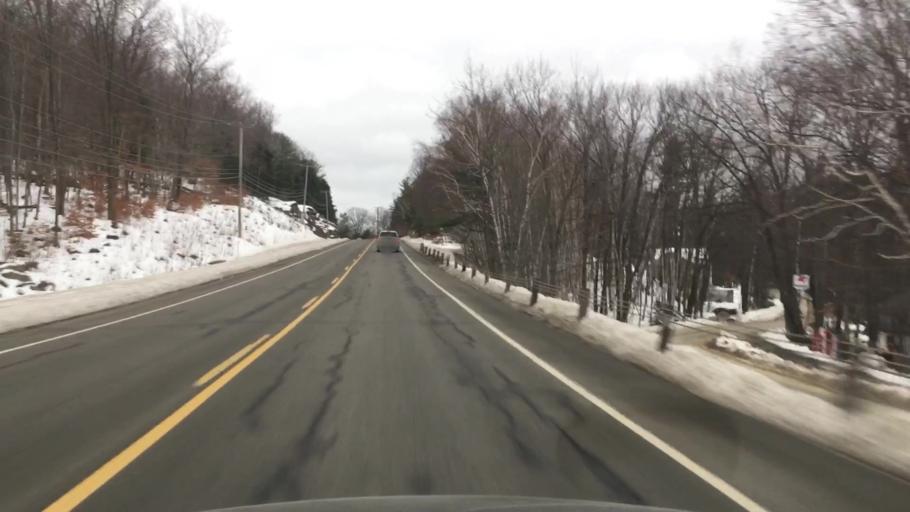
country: US
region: New Hampshire
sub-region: Merrimack County
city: Newbury
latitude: 43.3338
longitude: -72.0485
